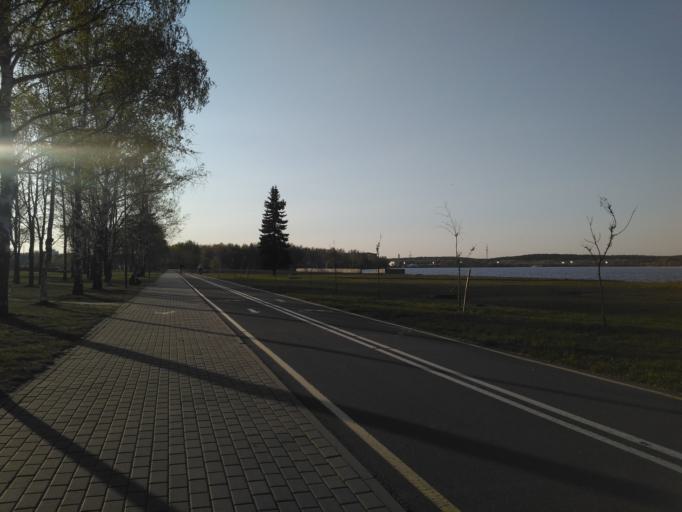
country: BY
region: Minsk
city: Zhdanovichy
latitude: 53.9441
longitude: 27.4633
